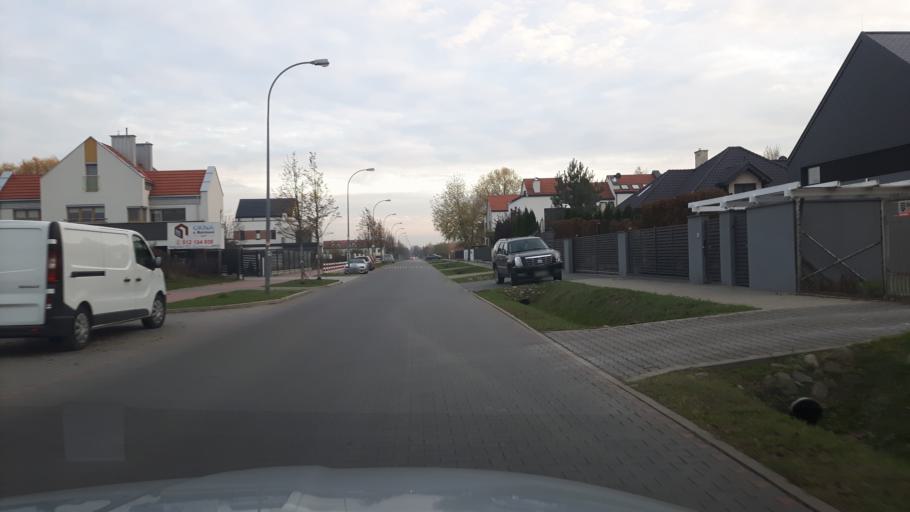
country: PL
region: Masovian Voivodeship
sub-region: Warszawa
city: Wilanow
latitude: 52.1802
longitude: 21.1065
